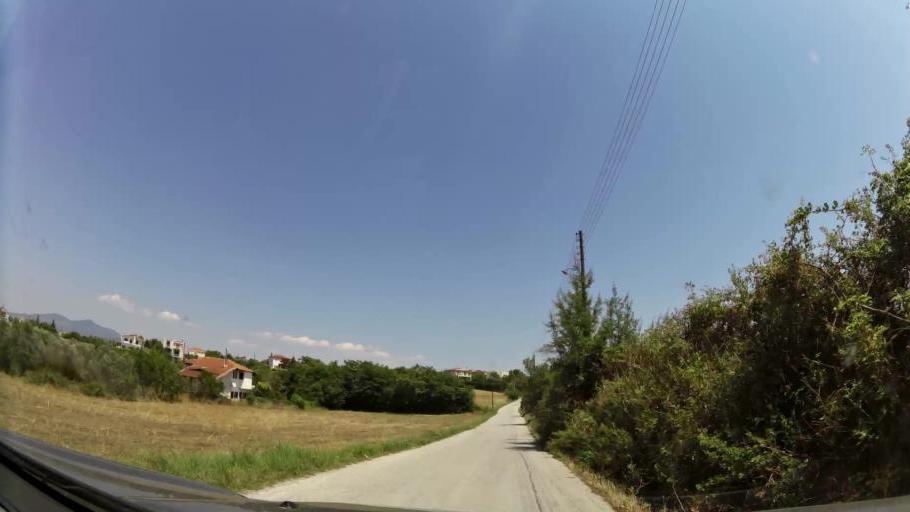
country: GR
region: Central Macedonia
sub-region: Nomos Thessalonikis
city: Trilofos
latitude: 40.4699
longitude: 22.9756
